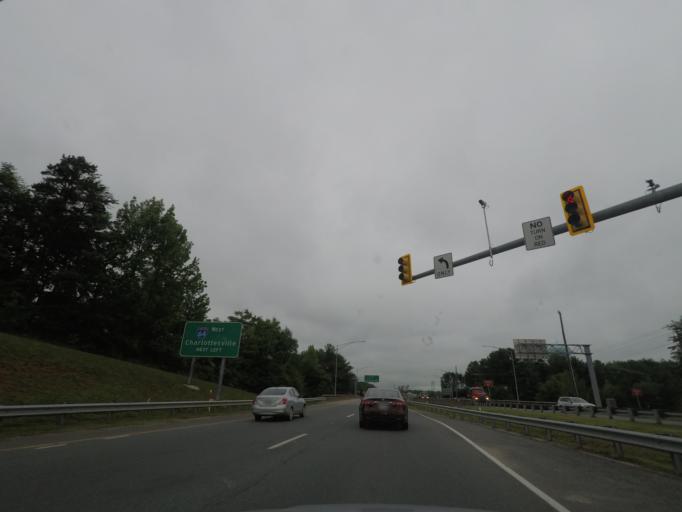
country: US
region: Virginia
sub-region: Fluvanna County
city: Palmyra
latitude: 37.9764
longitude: -78.2145
